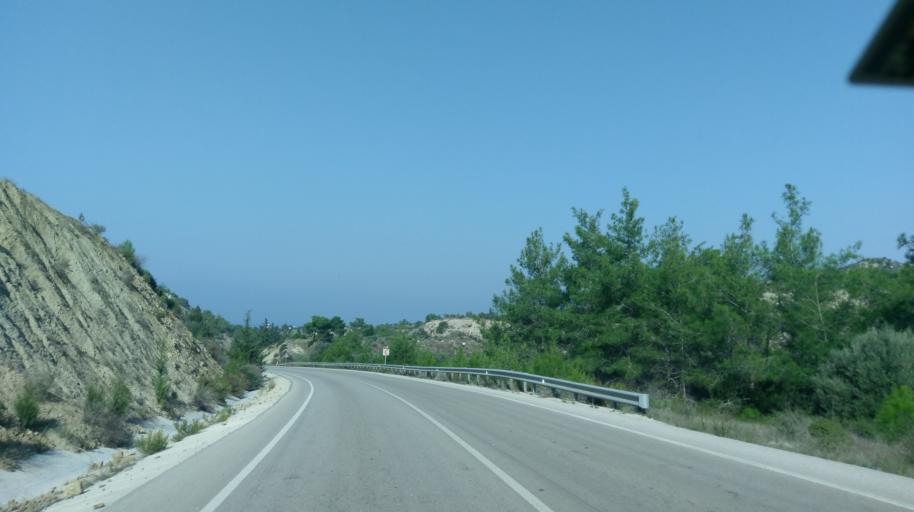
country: CY
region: Ammochostos
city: Lefkonoiko
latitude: 35.3607
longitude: 33.7115
